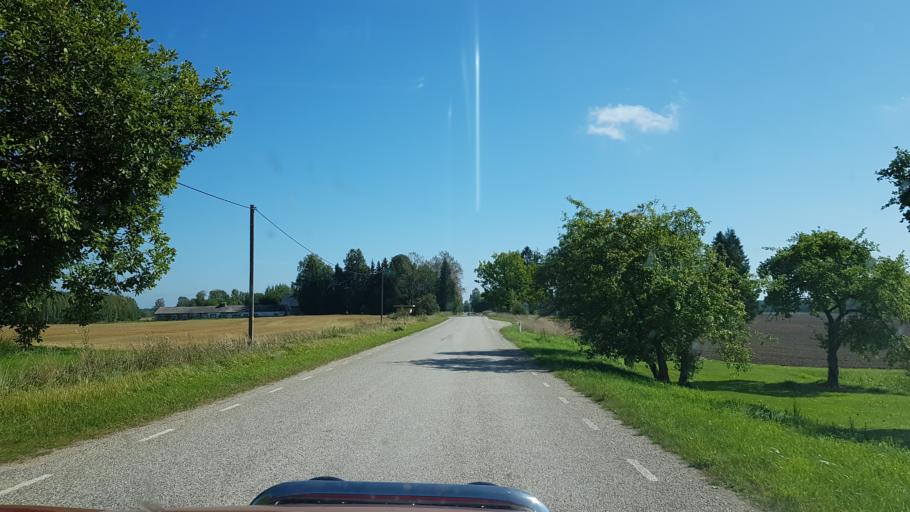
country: EE
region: Polvamaa
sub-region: Raepina vald
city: Rapina
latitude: 58.2297
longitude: 27.3791
